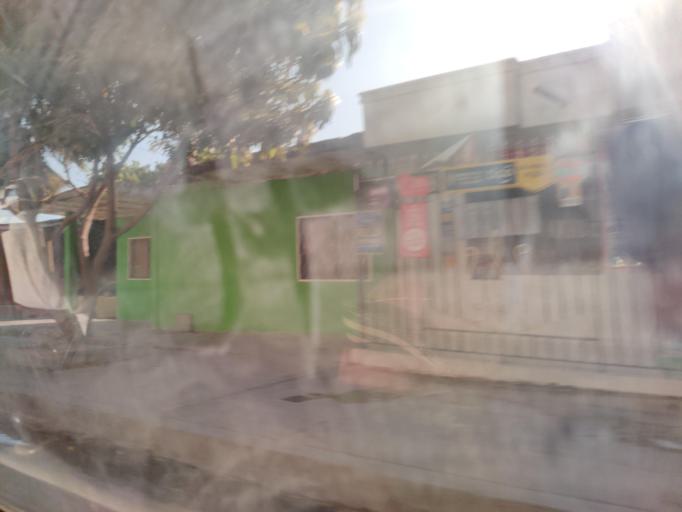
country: CO
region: Atlantico
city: Soledad
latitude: 10.9131
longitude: -74.8046
